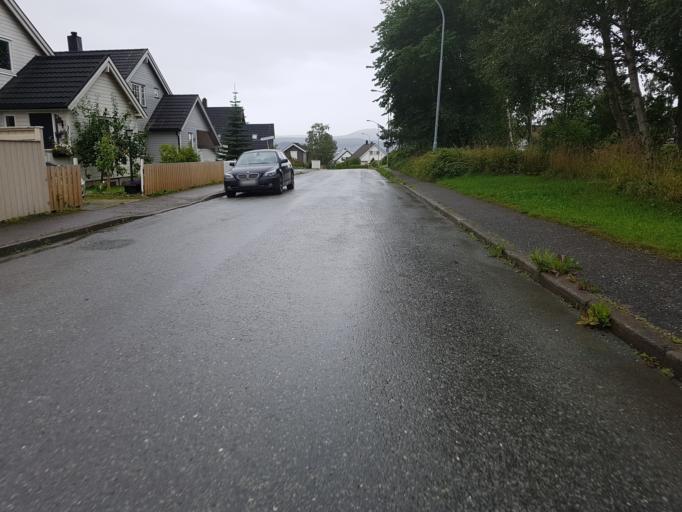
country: NO
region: Sor-Trondelag
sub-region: Trondheim
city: Trondheim
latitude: 63.4017
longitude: 10.4514
